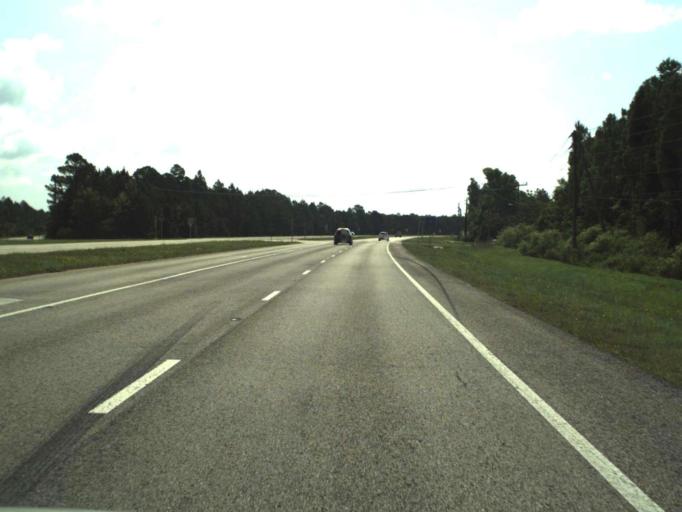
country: US
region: Florida
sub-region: Volusia County
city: Samsula-Spruce Creek
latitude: 29.0248
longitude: -81.1263
